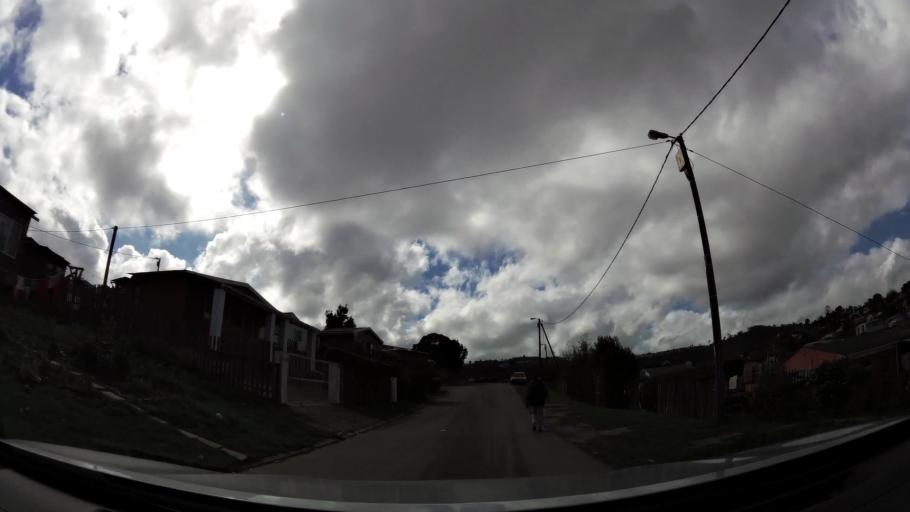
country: ZA
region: Western Cape
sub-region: Eden District Municipality
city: Knysna
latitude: -34.0517
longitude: 23.0923
